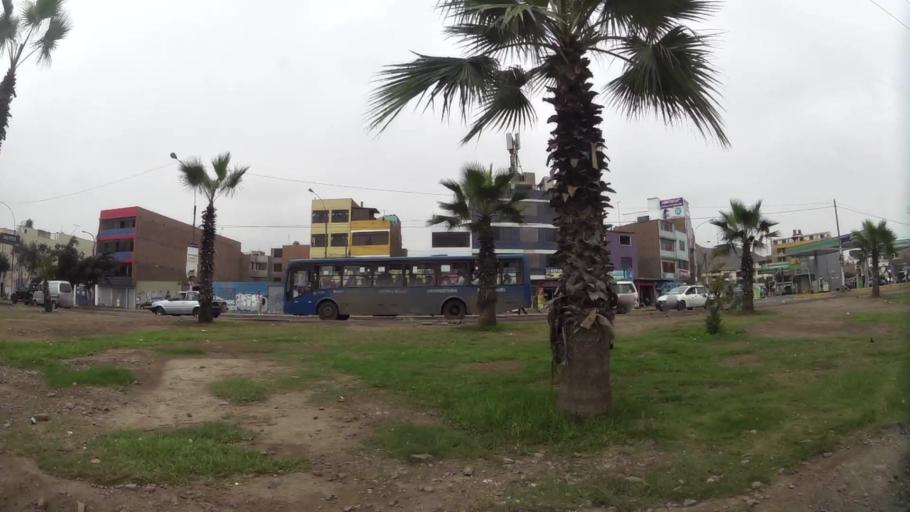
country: PE
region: Lima
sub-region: Lima
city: Independencia
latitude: -11.9950
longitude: -77.0842
